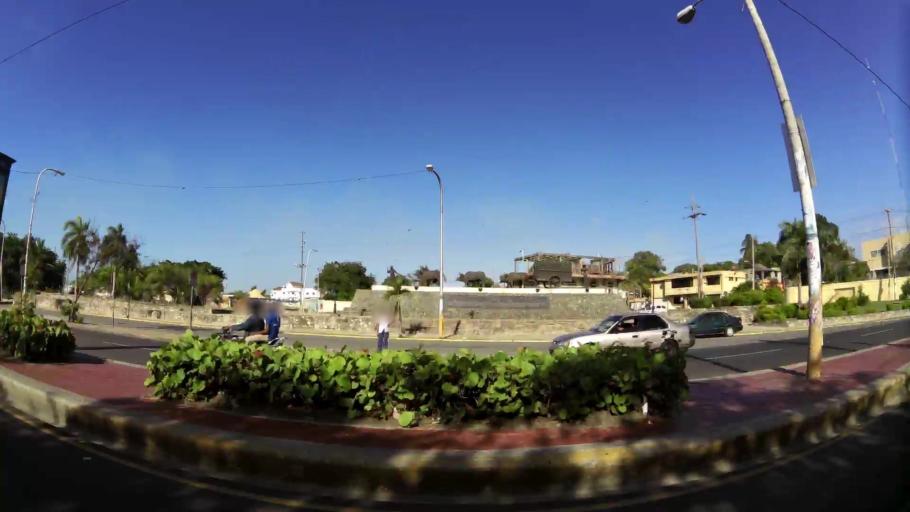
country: DO
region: Nacional
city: San Carlos
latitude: 18.4793
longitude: -69.8778
